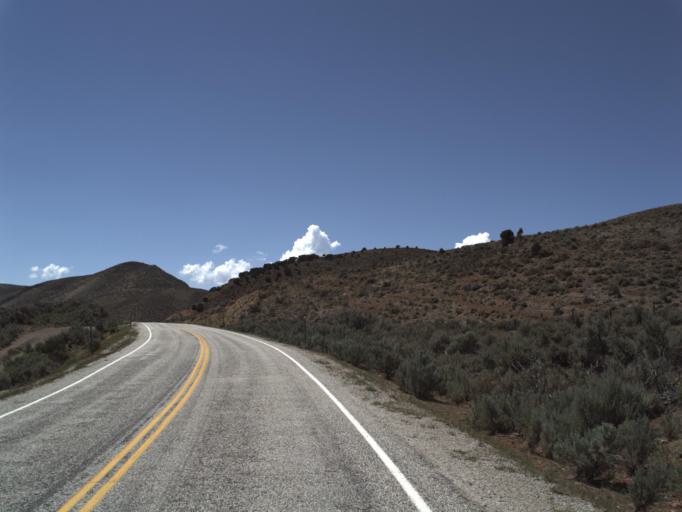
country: US
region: Utah
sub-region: Rich County
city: Randolph
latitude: 41.5029
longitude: -111.2853
